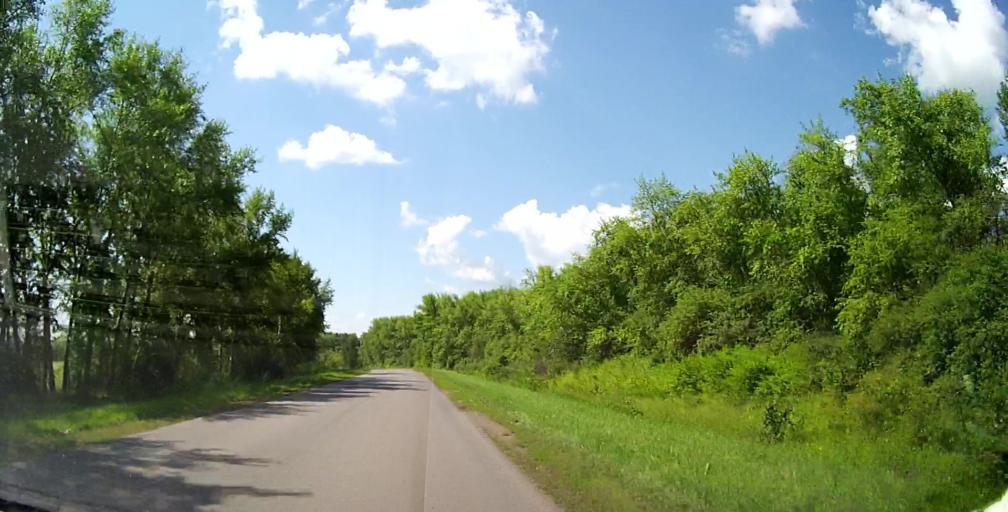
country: RU
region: Lipetsk
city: Chaplygin
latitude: 53.3080
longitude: 39.9539
